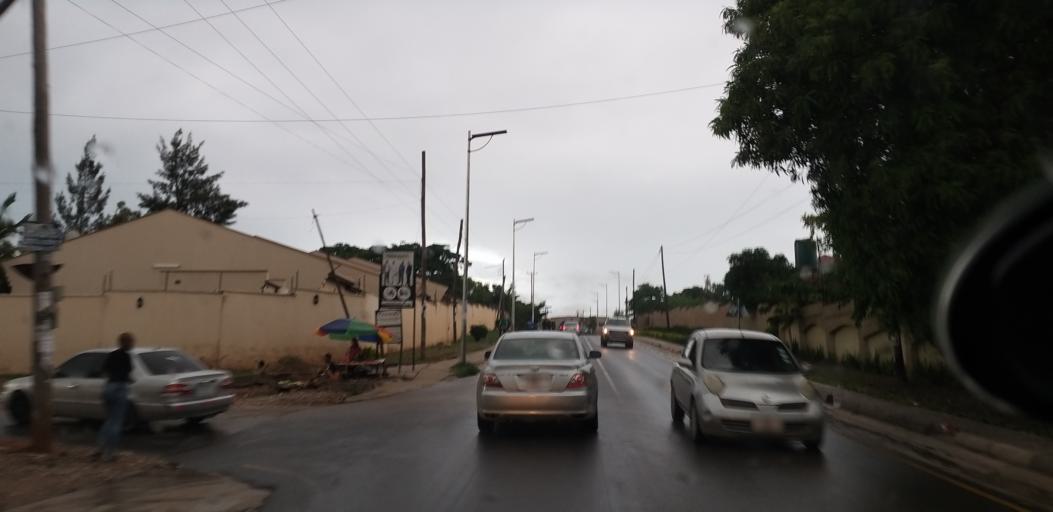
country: ZM
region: Lusaka
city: Lusaka
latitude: -15.4164
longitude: 28.3617
